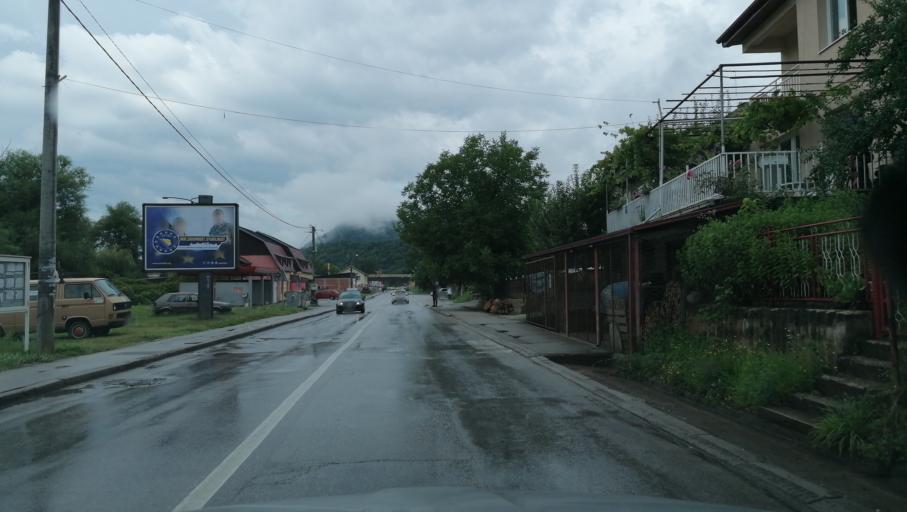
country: BA
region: Republika Srpska
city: Visegrad
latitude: 43.7880
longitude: 19.2960
